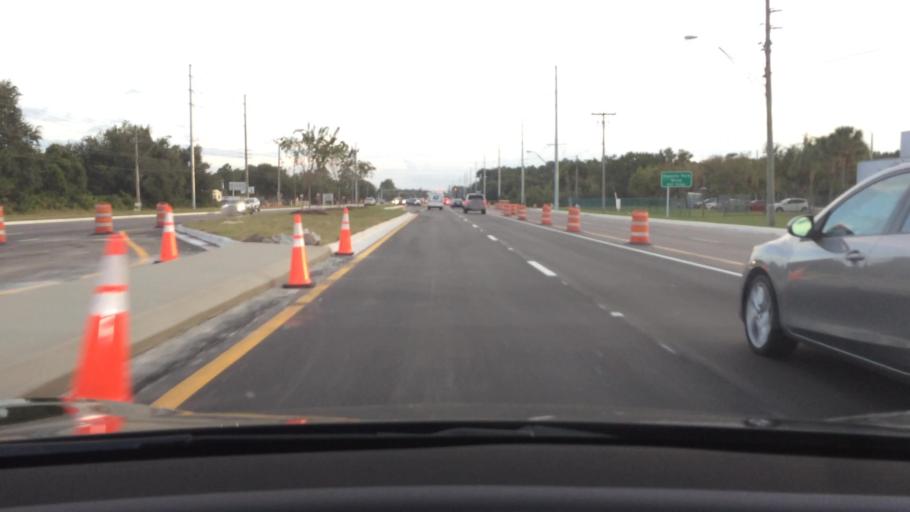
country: US
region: Florida
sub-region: Hillsborough County
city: Pebble Creek
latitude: 28.1582
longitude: -82.3535
